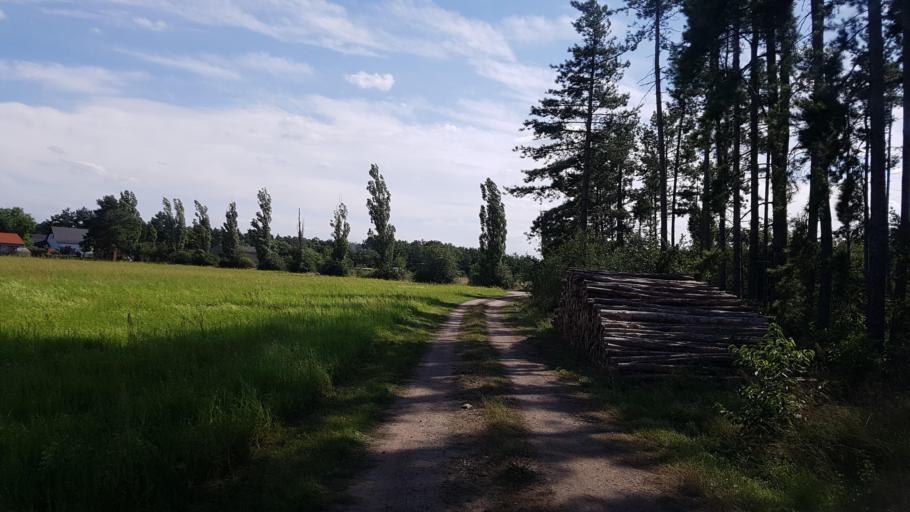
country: DE
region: Brandenburg
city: Muhlberg
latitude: 51.4480
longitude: 13.2906
